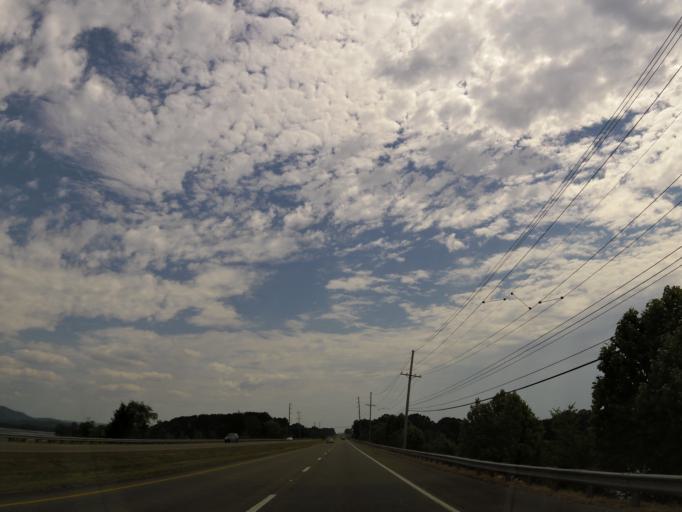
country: US
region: Alabama
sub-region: Jackson County
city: Stevenson
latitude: 34.8452
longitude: -85.8290
